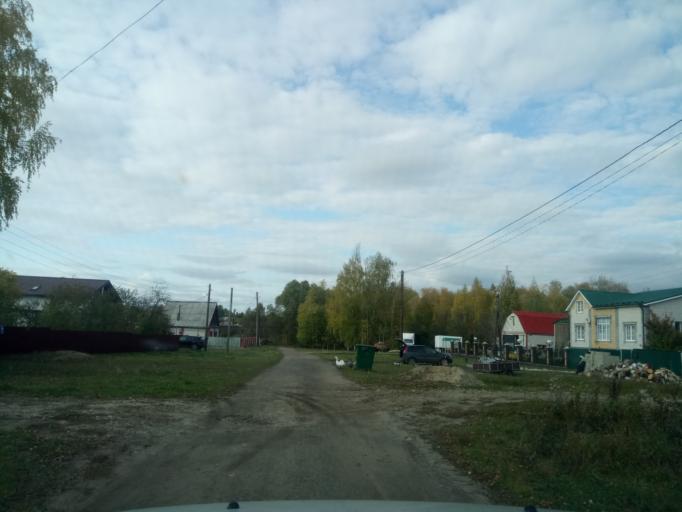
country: RU
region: Nizjnij Novgorod
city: Bol'shoye Boldino
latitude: 54.9912
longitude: 45.3179
